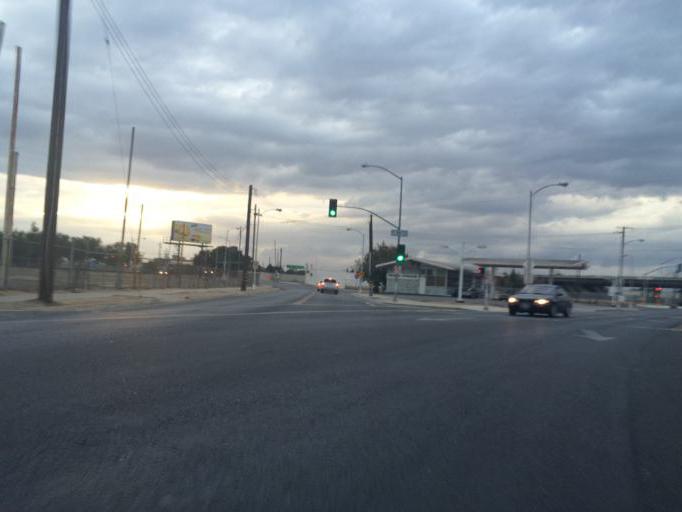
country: US
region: California
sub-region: Fresno County
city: Fresno
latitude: 36.7437
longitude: -119.8045
